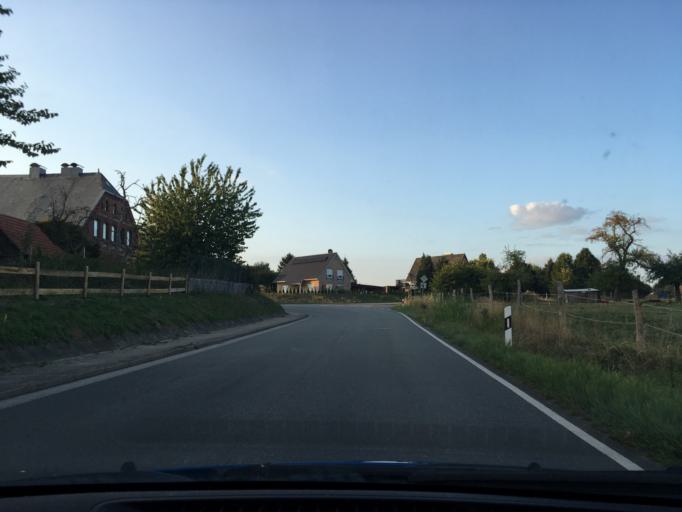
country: DE
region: Lower Saxony
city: Bleckede
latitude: 53.2557
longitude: 10.7634
